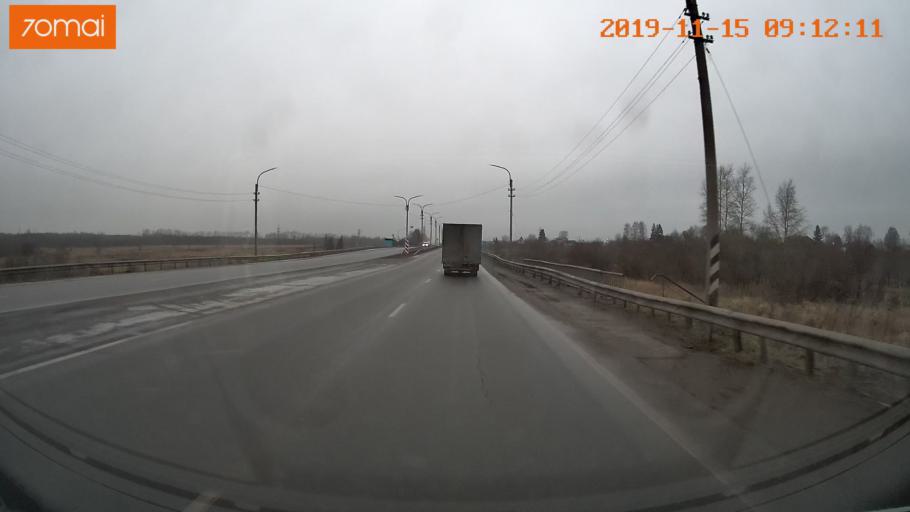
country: RU
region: Vologda
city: Tonshalovo
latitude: 59.2053
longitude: 37.9396
